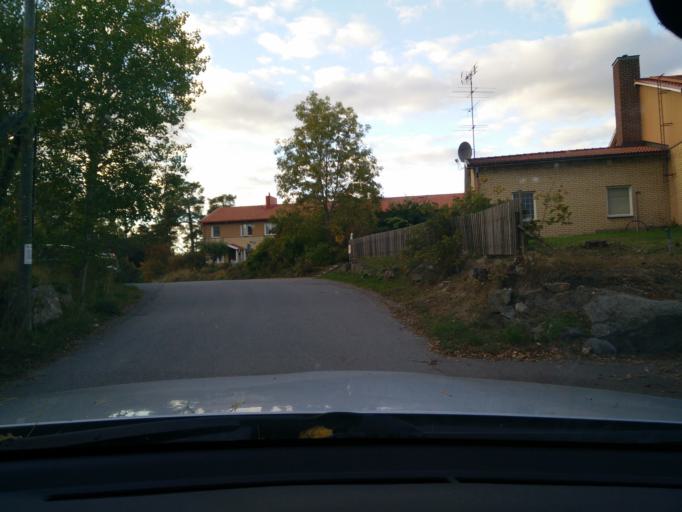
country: SE
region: Stockholm
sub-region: Stockholms Kommun
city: Kista
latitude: 59.4154
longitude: 17.9433
